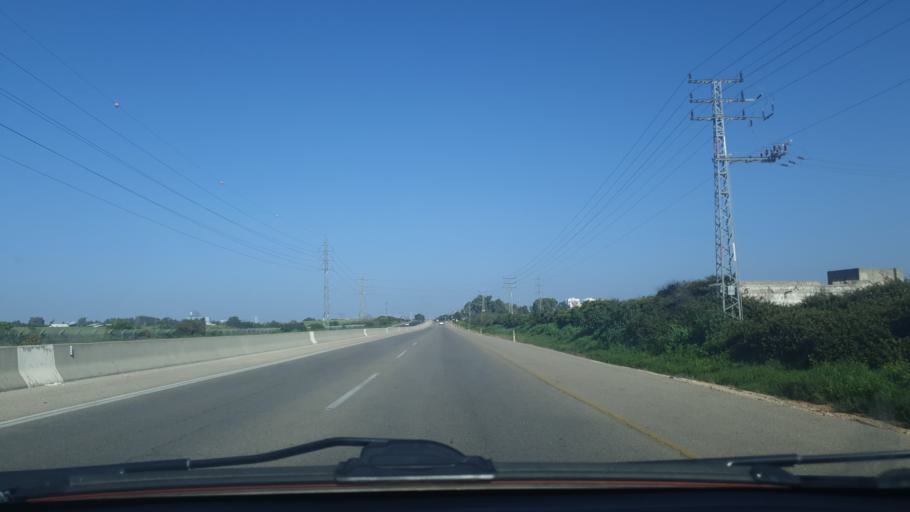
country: IL
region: Central District
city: Kefar Habad
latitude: 31.9816
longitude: 34.8349
